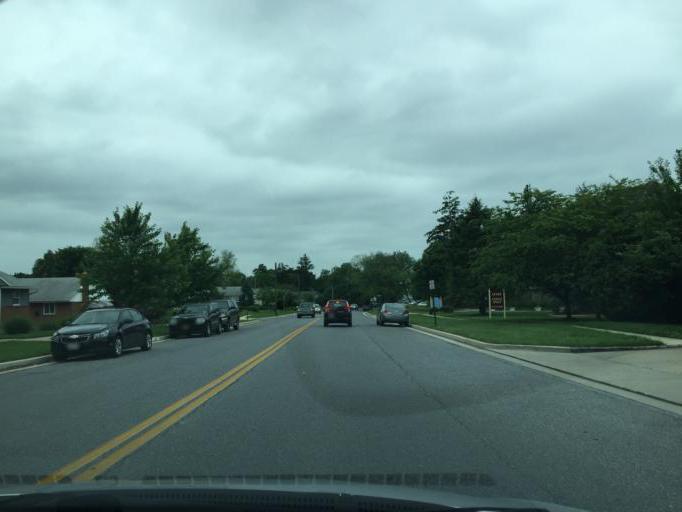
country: US
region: Maryland
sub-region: Baltimore County
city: Timonium
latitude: 39.4426
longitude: -76.6234
